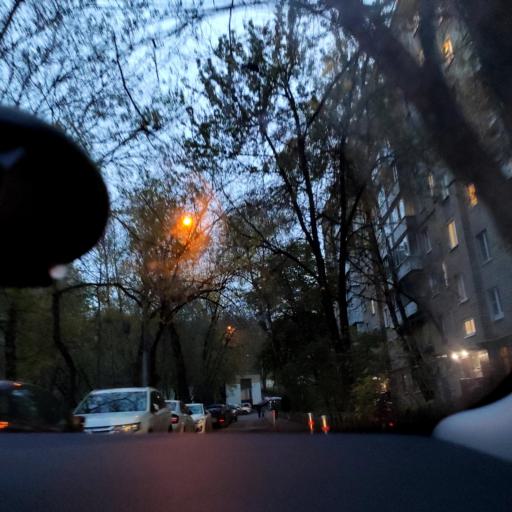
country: RU
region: Moskovskaya
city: Kozhukhovo
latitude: 55.6813
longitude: 37.6529
